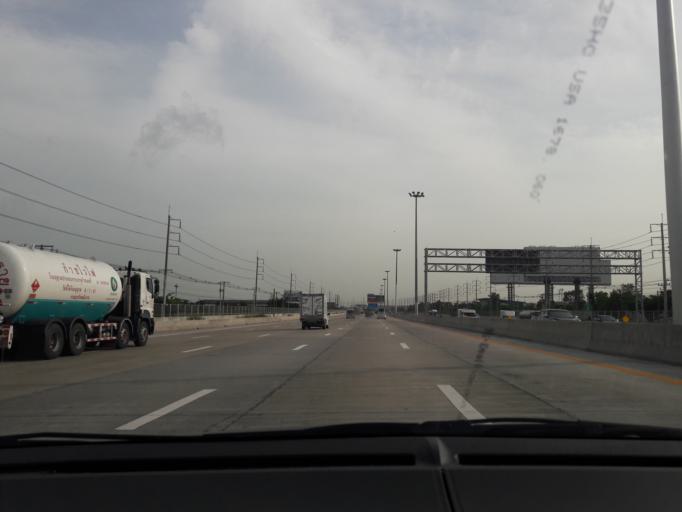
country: TH
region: Pathum Thani
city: Thanyaburi
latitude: 13.9815
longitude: 100.7132
